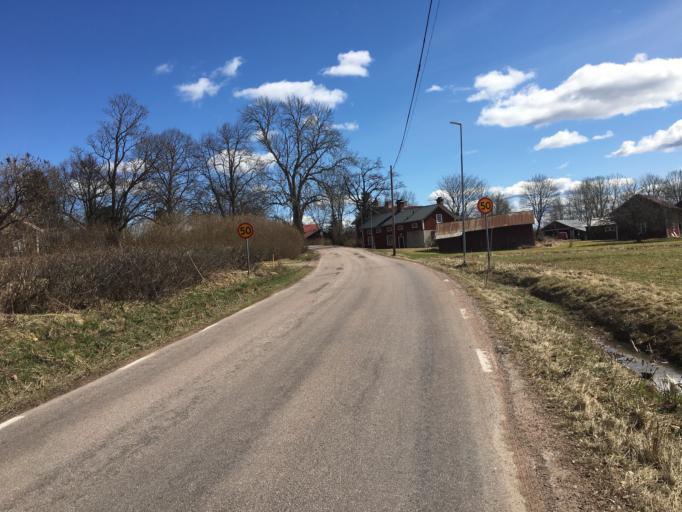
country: SE
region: Gaevleborg
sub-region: Hofors Kommun
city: Hofors
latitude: 60.5149
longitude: 16.4434
